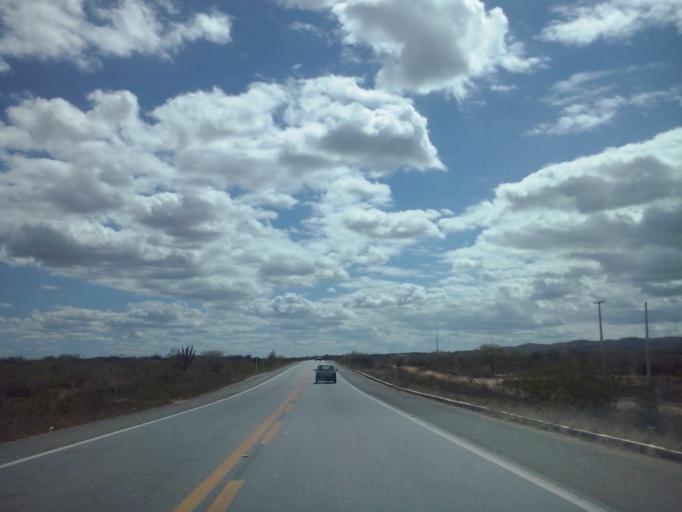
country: BR
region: Paraiba
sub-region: Soledade
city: Soledade
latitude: -7.0494
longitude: -36.3836
